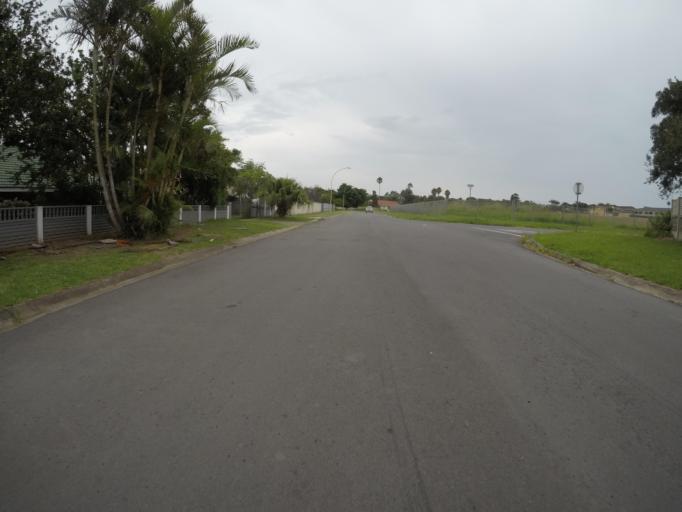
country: ZA
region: Eastern Cape
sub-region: Buffalo City Metropolitan Municipality
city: East London
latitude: -32.9996
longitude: 27.8556
